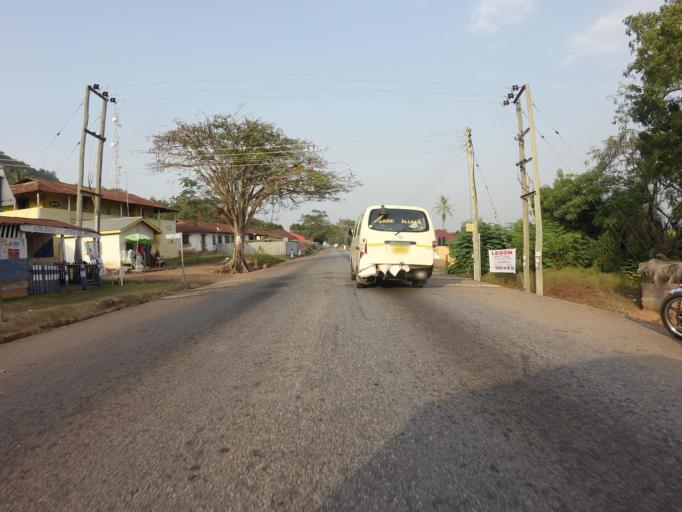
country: GH
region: Volta
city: Ho
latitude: 6.5423
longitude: 0.2883
